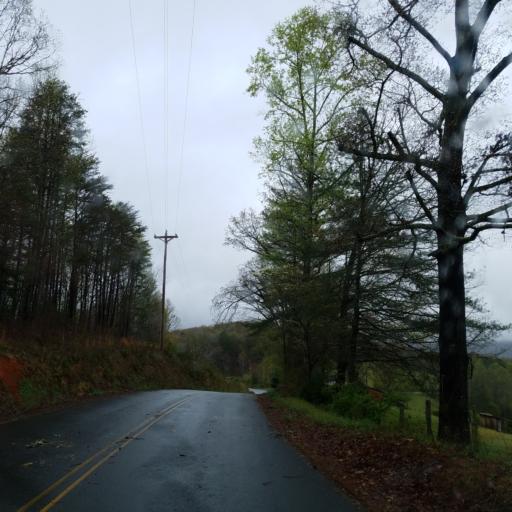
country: US
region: Georgia
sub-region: Fannin County
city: Blue Ridge
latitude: 34.8463
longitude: -84.2327
